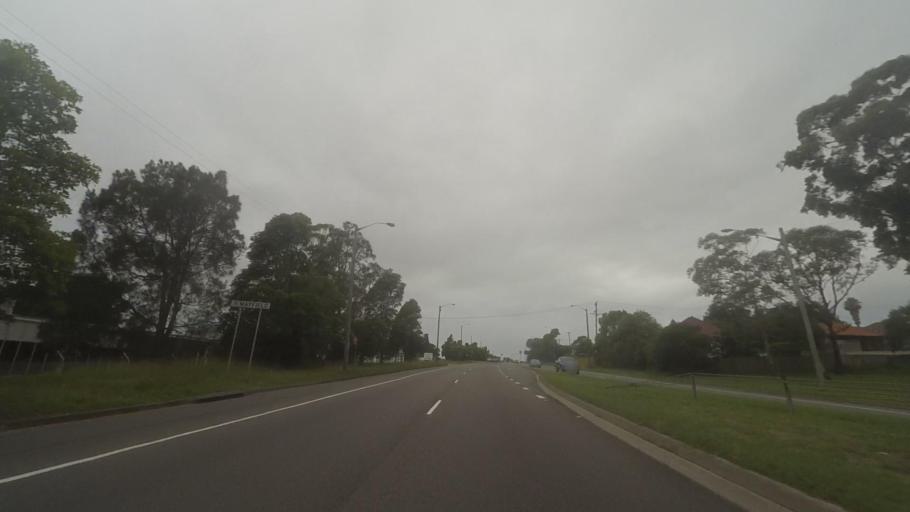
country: AU
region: New South Wales
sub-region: Newcastle
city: Mayfield West
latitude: -32.8874
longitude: 151.7348
